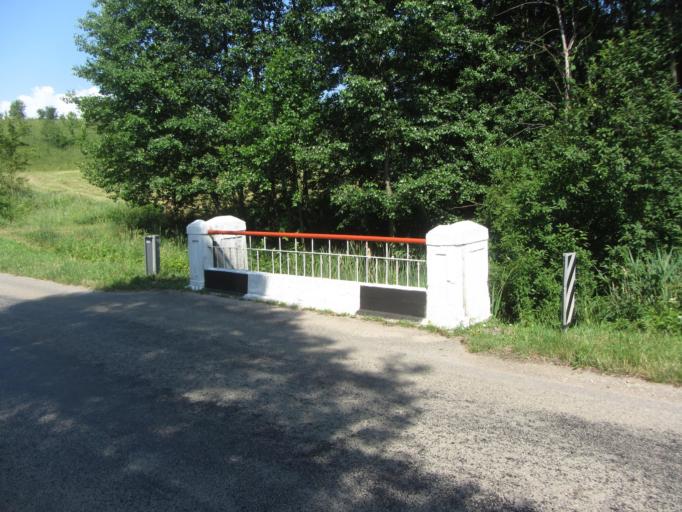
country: LT
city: Veisiejai
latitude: 54.1648
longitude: 23.6566
